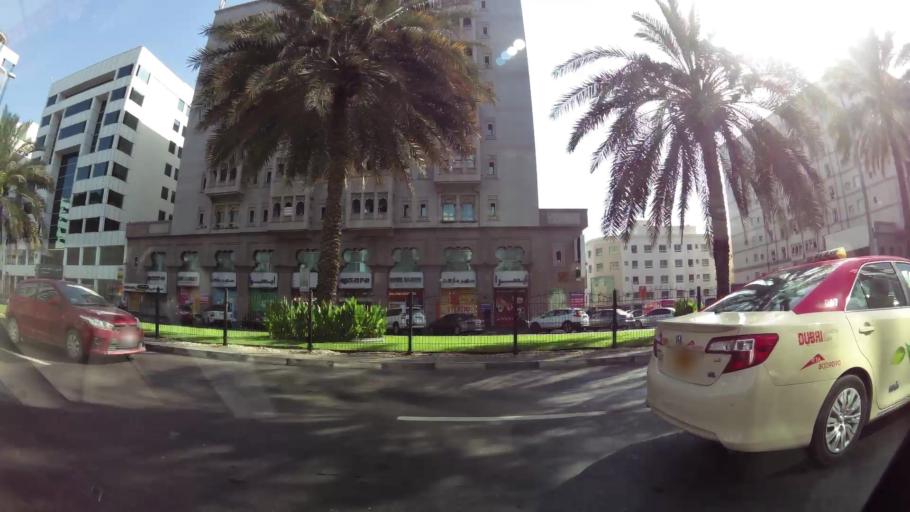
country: AE
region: Ash Shariqah
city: Sharjah
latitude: 25.2569
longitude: 55.2998
